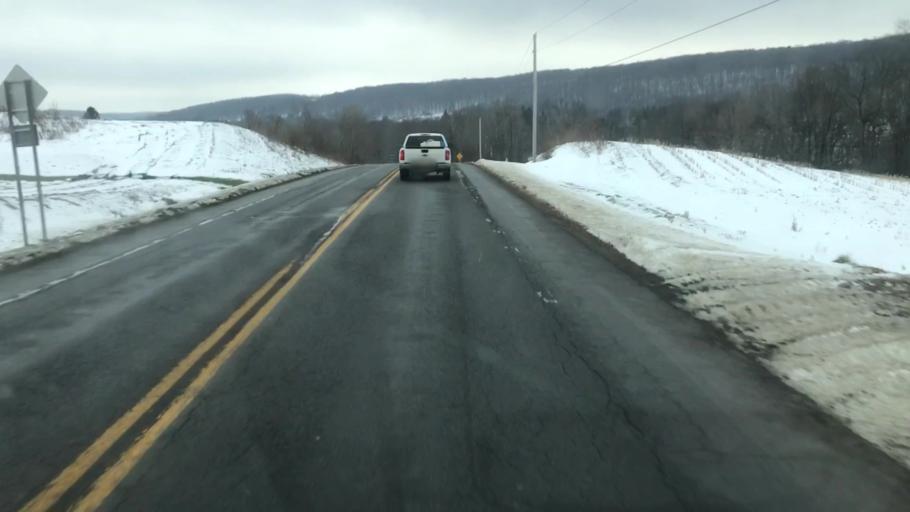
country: US
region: New York
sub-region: Tompkins County
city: Groton
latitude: 42.6848
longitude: -76.3012
